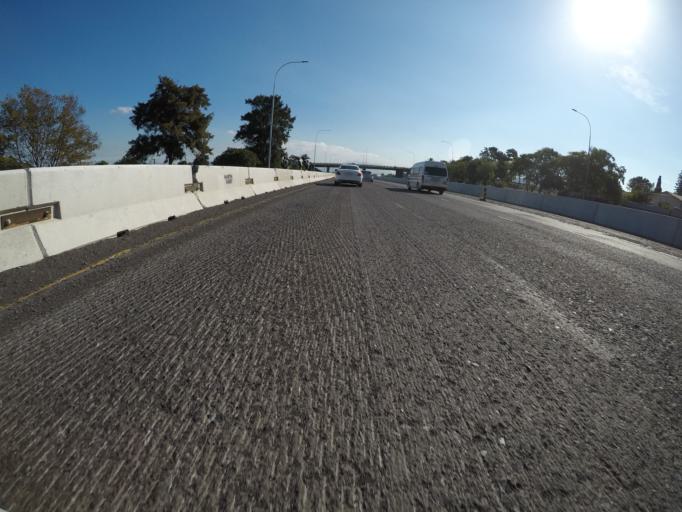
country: ZA
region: Western Cape
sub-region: City of Cape Town
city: Kraaifontein
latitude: -33.8817
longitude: 18.6480
